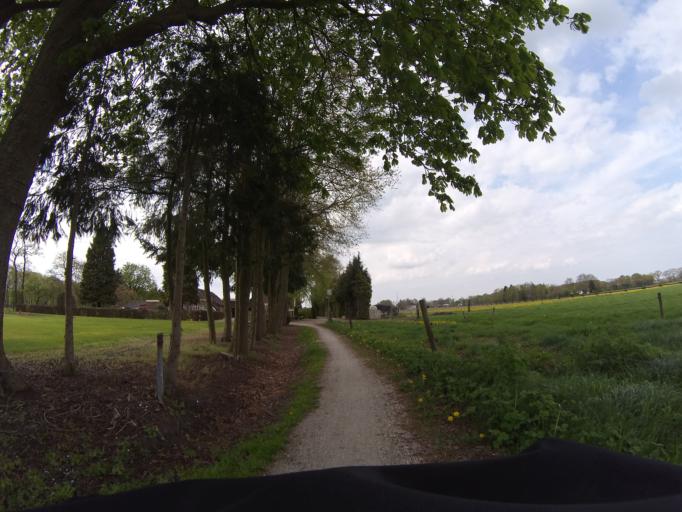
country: NL
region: Gelderland
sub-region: Gemeente Oldebroek
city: Oldebroek
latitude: 52.4458
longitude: 5.9203
